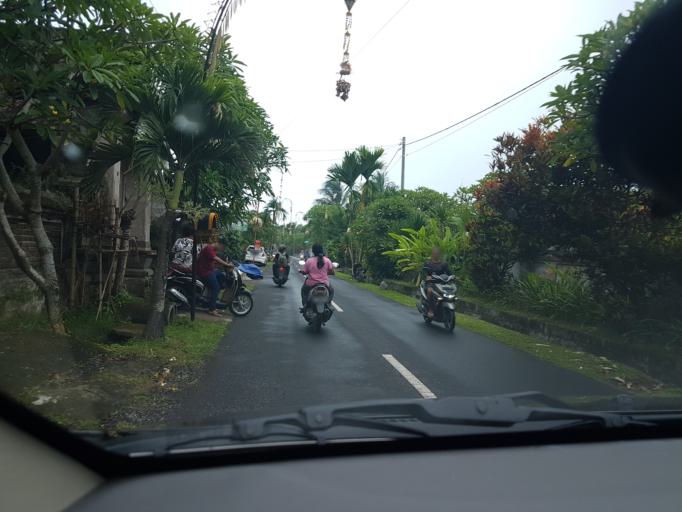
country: ID
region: Bali
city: Banjar Tebongkang
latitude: -8.5330
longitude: 115.2375
